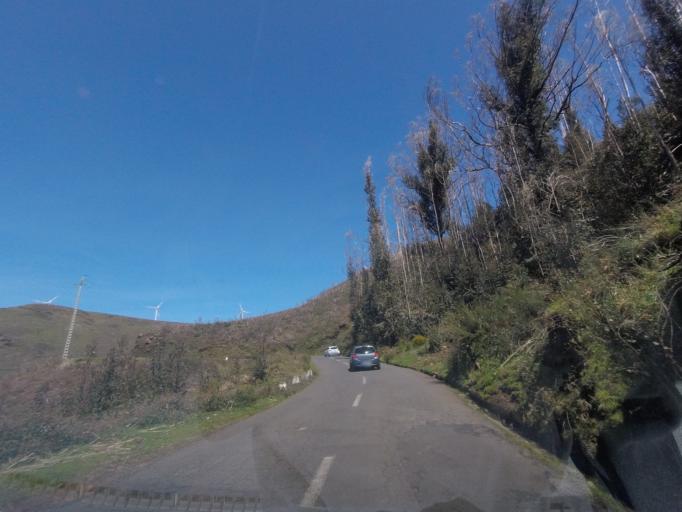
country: PT
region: Madeira
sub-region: Calheta
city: Arco da Calheta
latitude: 32.7372
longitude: -17.1034
